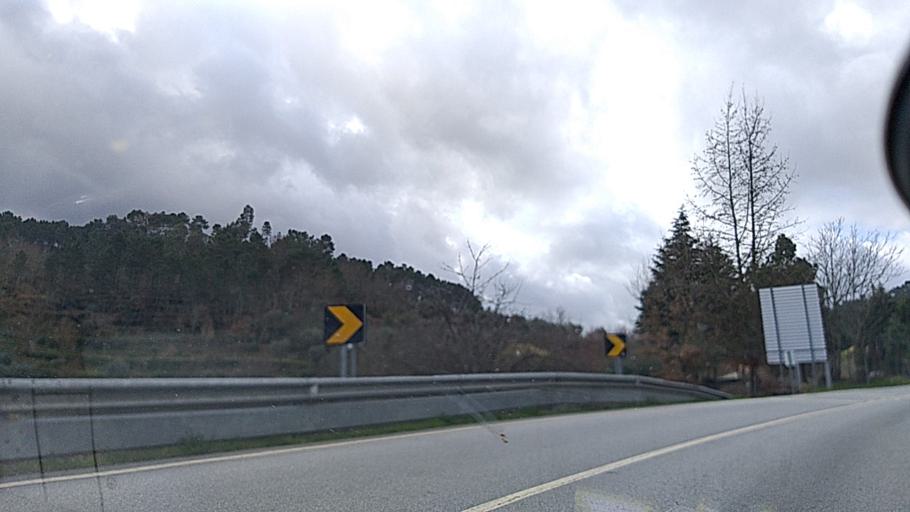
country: PT
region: Viseu
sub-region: Mangualde
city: Mangualde
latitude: 40.6445
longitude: -7.7351
